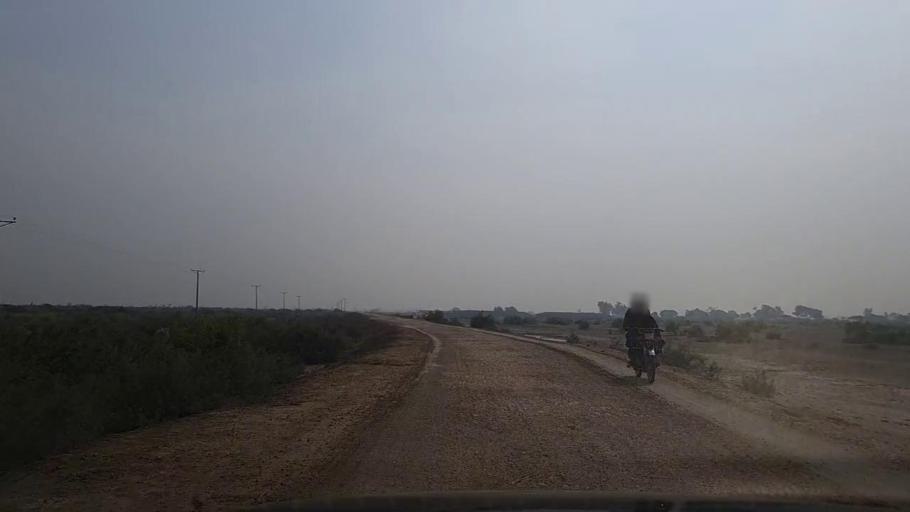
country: PK
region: Sindh
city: Mirpur Sakro
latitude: 24.3931
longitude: 67.7513
